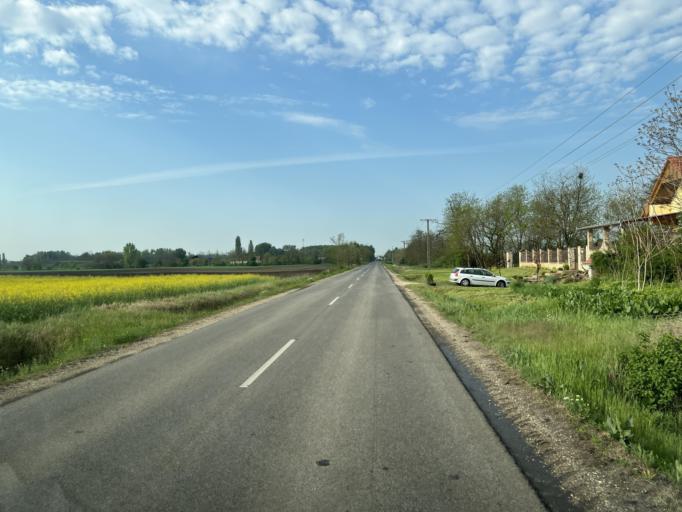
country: HU
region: Pest
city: Abony
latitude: 47.2128
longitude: 20.0138
